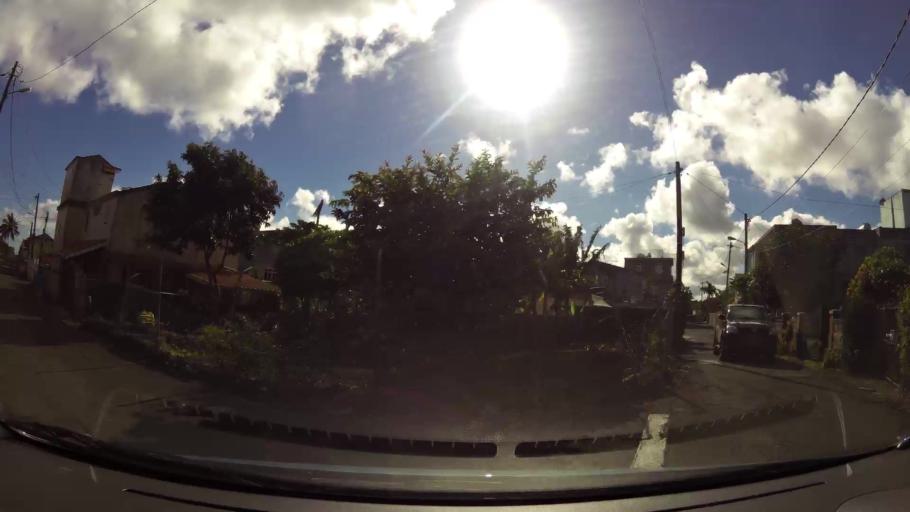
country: MU
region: Plaines Wilhems
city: Curepipe
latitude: -20.2977
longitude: 57.5183
